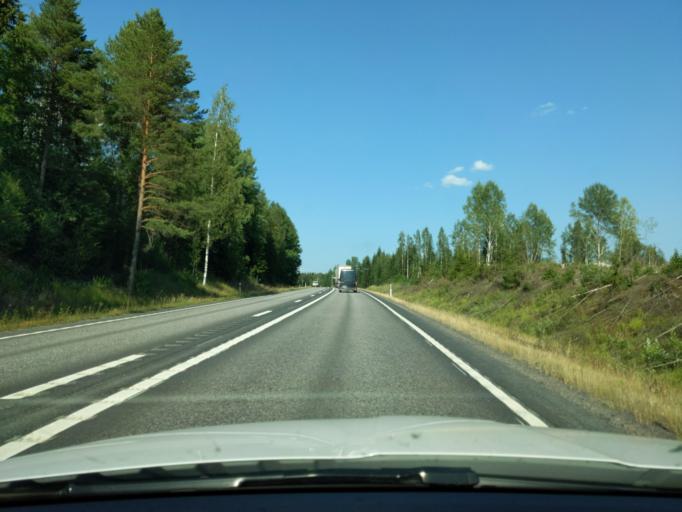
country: FI
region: Paijanne Tavastia
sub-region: Lahti
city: Jaervelae
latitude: 60.9130
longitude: 25.3486
